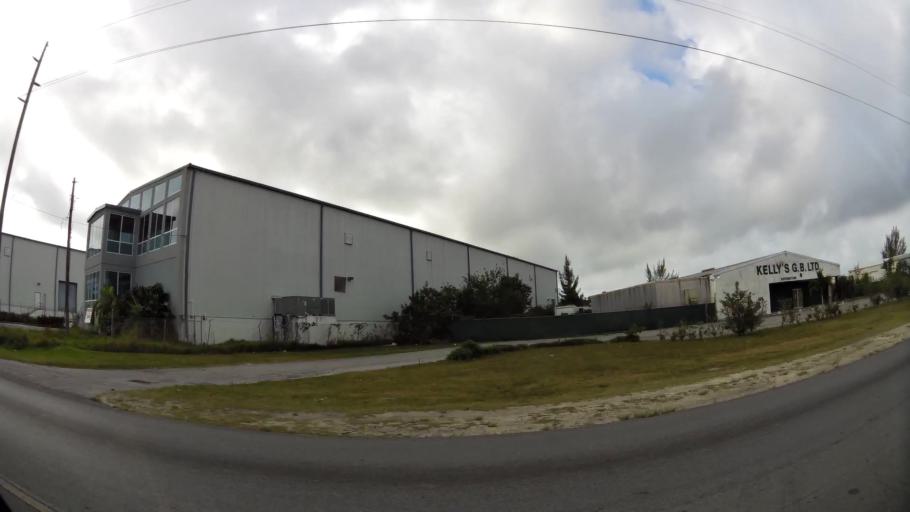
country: BS
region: Freeport
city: Freeport
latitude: 26.5365
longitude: -78.7160
